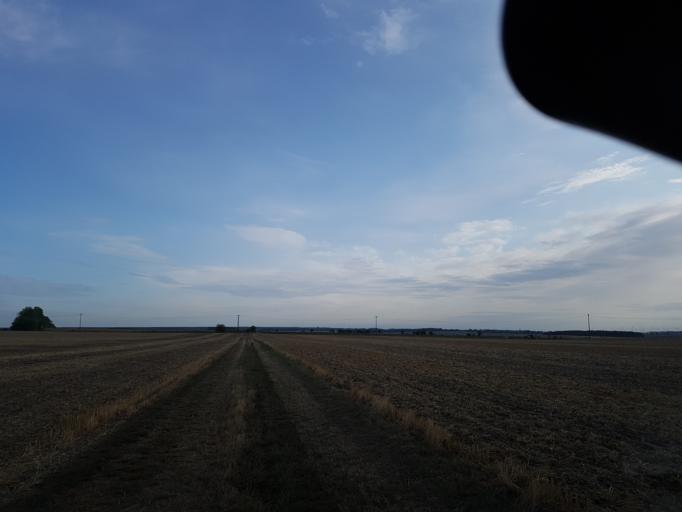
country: DE
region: Brandenburg
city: Niedergorsdorf
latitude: 51.9397
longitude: 13.0107
